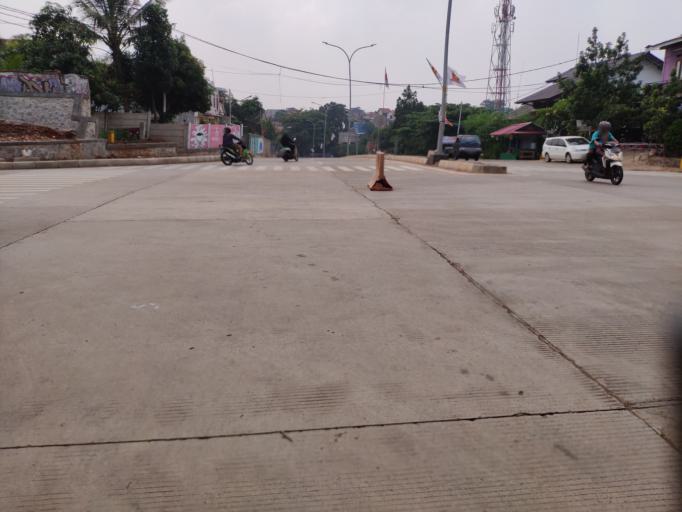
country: ID
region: West Java
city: Pamulang
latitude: -6.3245
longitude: 106.8026
